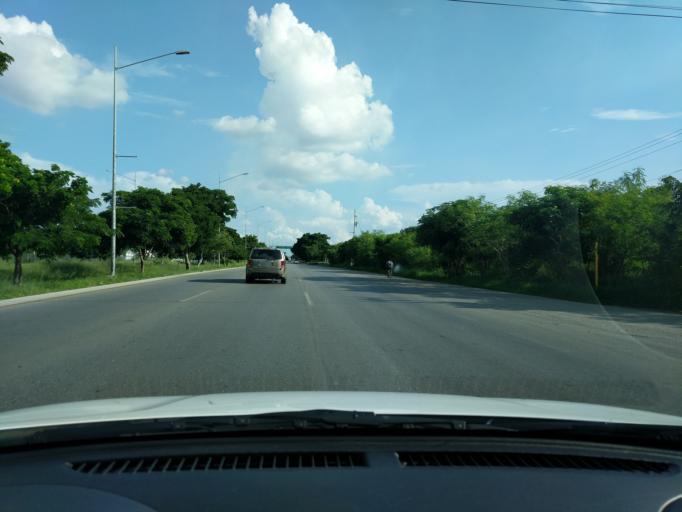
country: MX
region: Yucatan
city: Itzincab Palomeque
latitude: 20.9348
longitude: -89.6943
